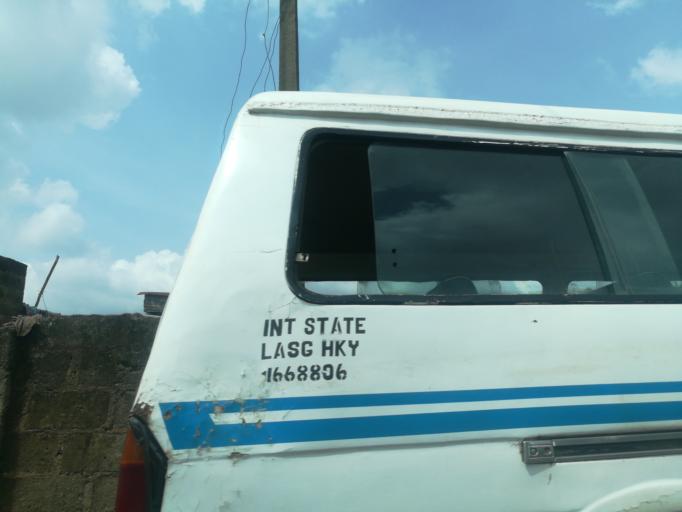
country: NG
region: Oyo
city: Ibadan
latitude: 7.4119
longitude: 3.9457
